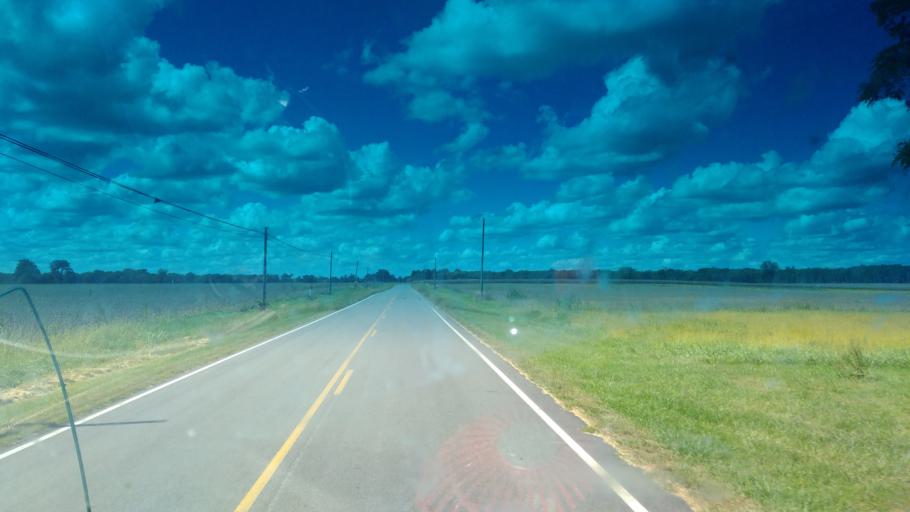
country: US
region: Ohio
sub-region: Union County
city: Marysville
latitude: 40.1847
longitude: -83.4539
